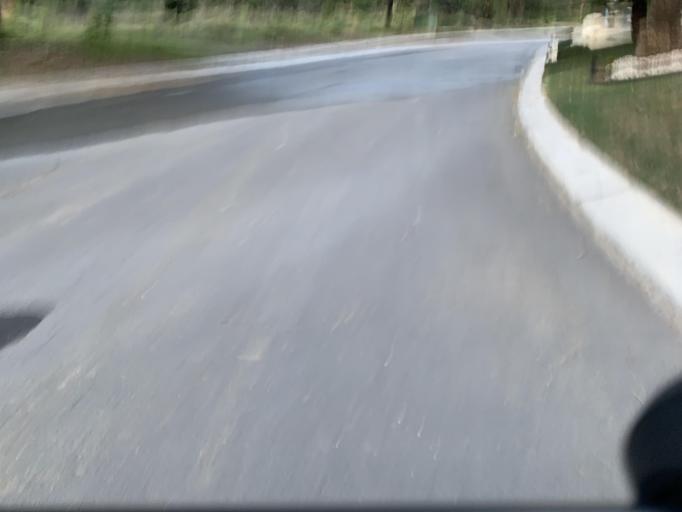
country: MX
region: Nuevo Leon
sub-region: Juarez
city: Bosques de San Pedro
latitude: 25.5207
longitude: -100.1961
